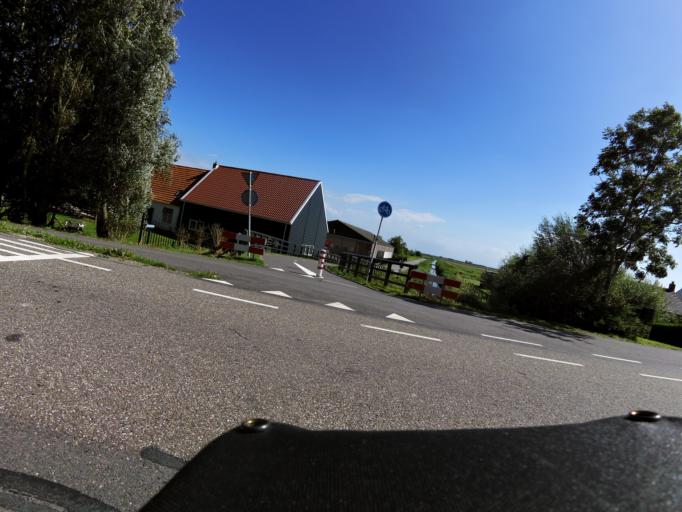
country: NL
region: South Holland
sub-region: Gemeente Goeree-Overflakkee
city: Dirksland
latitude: 51.7634
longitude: 4.0686
